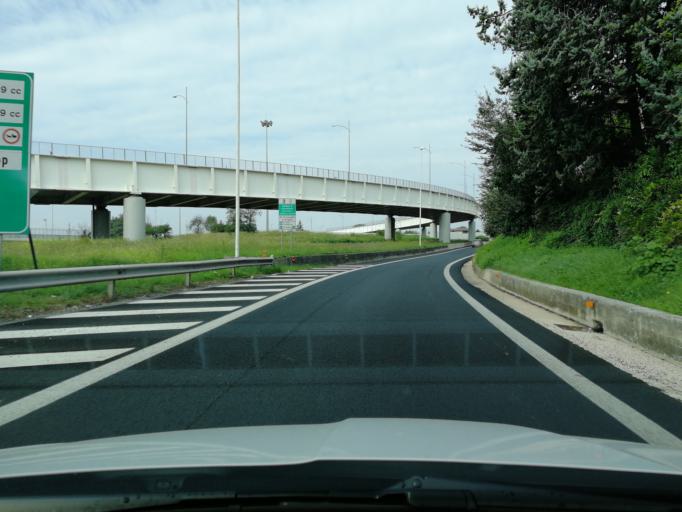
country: IT
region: Latium
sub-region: Citta metropolitana di Roma Capitale
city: Setteville
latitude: 41.9192
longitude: 12.6130
